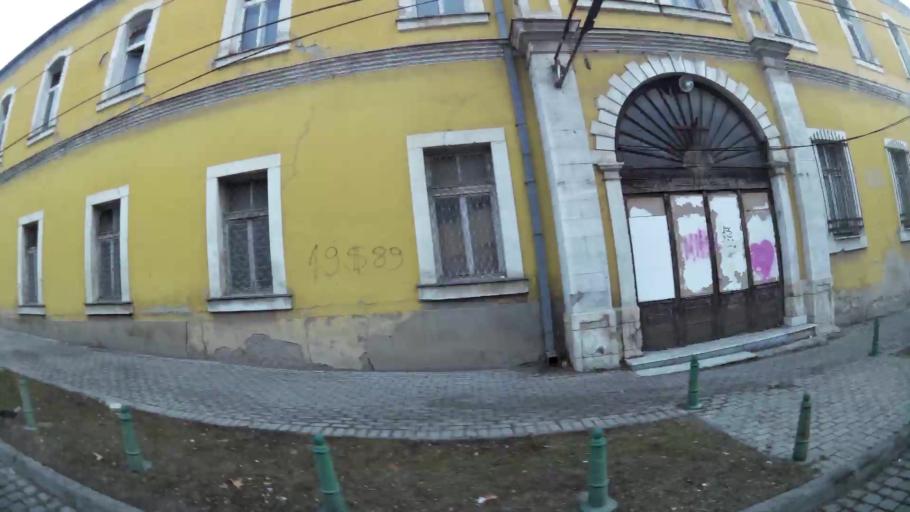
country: MK
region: Karpos
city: Skopje
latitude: 42.0014
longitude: 21.4348
